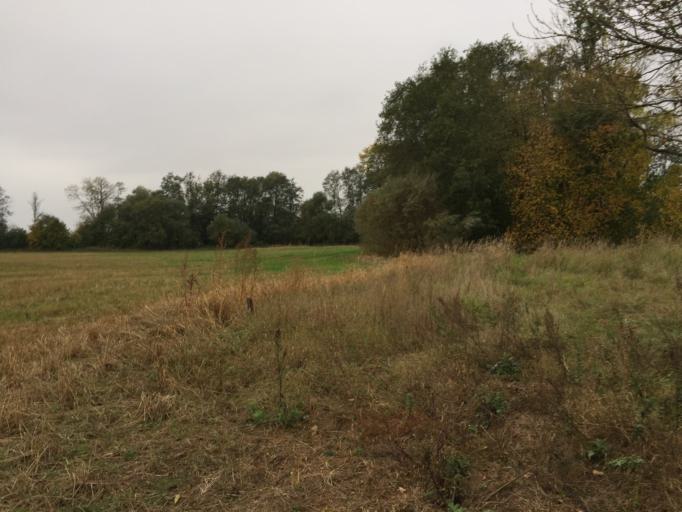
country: LV
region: Dobeles Rajons
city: Dobele
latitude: 56.6784
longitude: 23.4359
